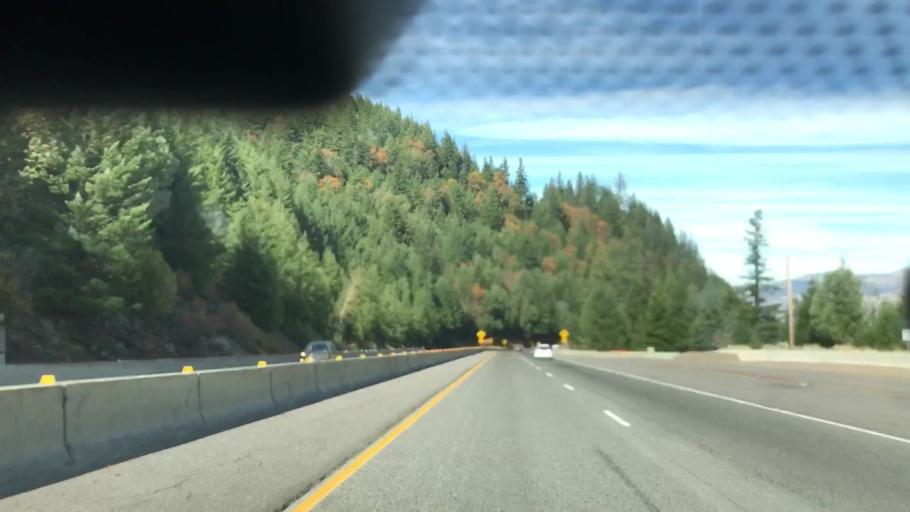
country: US
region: Oregon
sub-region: Jackson County
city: Ashland
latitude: 42.0858
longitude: -122.6013
